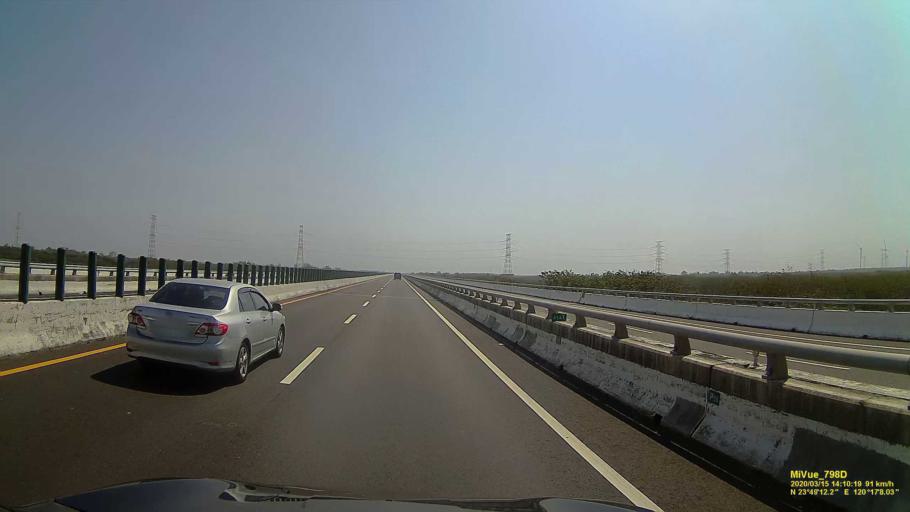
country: TW
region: Taiwan
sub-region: Yunlin
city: Douliu
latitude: 23.8196
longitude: 120.2854
